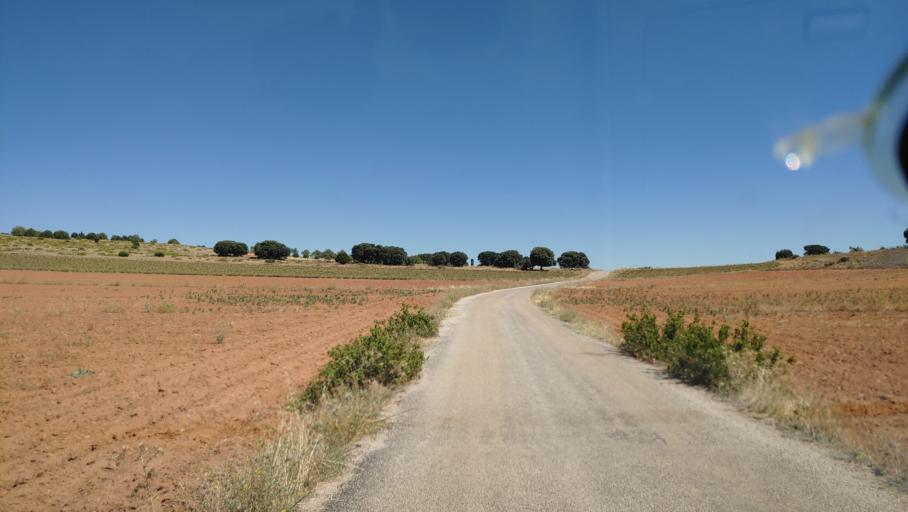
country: ES
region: Castille-La Mancha
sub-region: Provincia de Albacete
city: Ossa de Montiel
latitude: 38.9333
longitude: -2.7674
